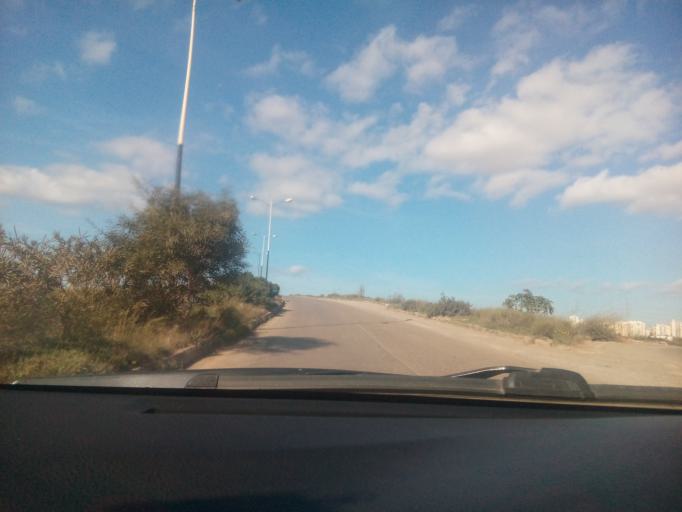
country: DZ
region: Oran
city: Bir el Djir
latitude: 35.6820
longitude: -0.5695
